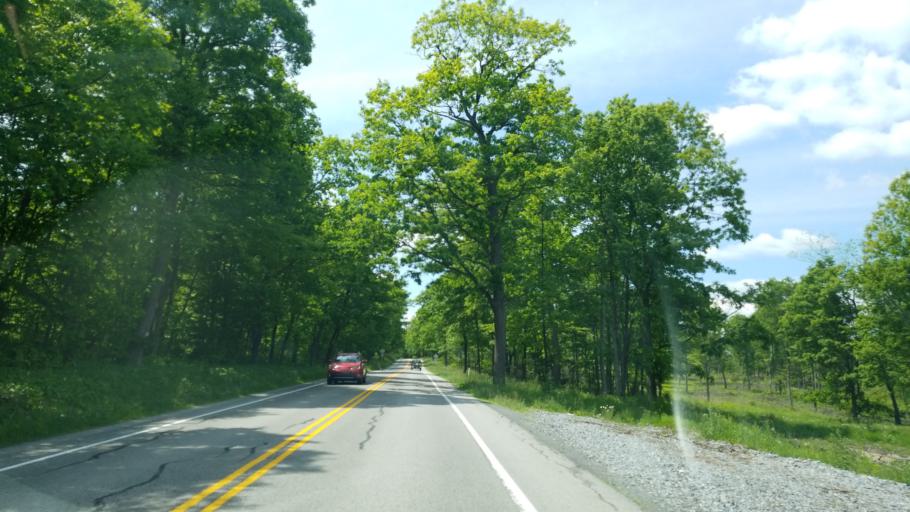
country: US
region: Pennsylvania
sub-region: Blair County
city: Tipton
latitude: 40.7047
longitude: -78.3088
